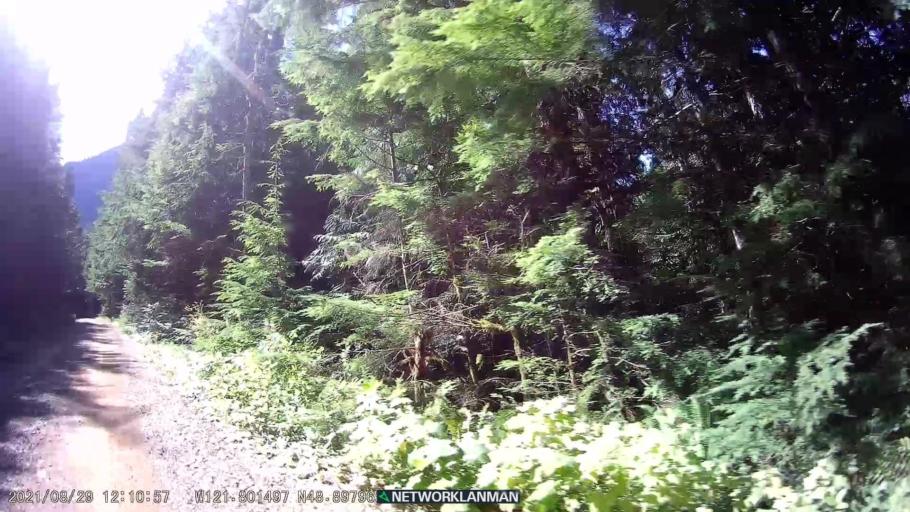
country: CA
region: British Columbia
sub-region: Fraser Valley Regional District
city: Chilliwack
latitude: 48.8979
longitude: -121.8015
